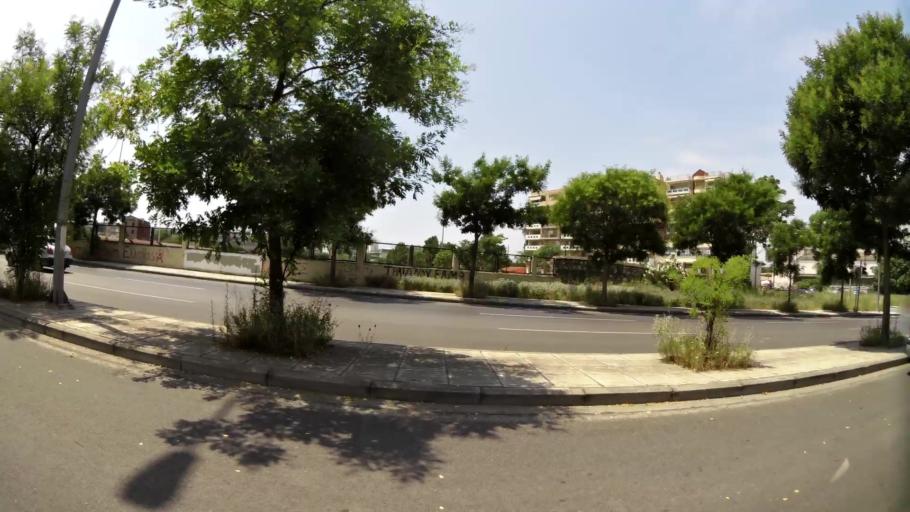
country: GR
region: Central Macedonia
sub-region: Nomos Thessalonikis
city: Ampelokipoi
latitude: 40.6451
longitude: 22.9191
